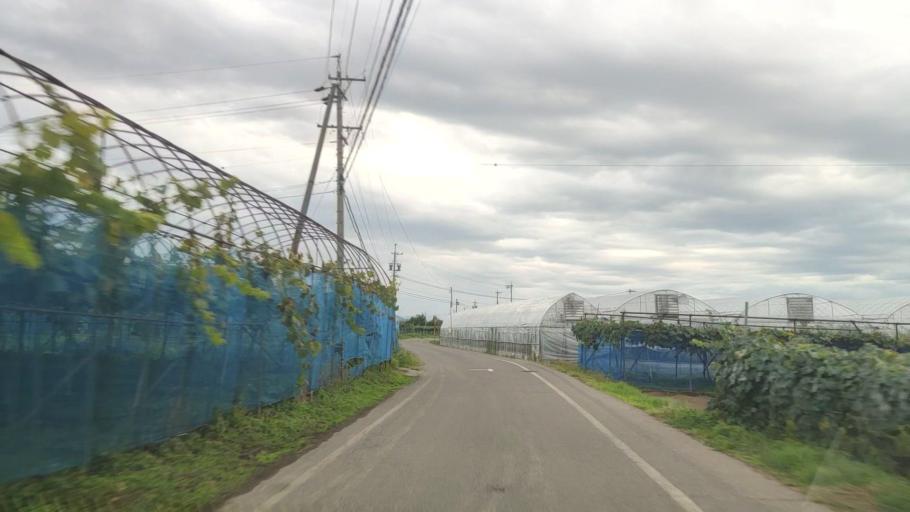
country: JP
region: Nagano
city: Nakano
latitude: 36.7673
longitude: 138.3888
